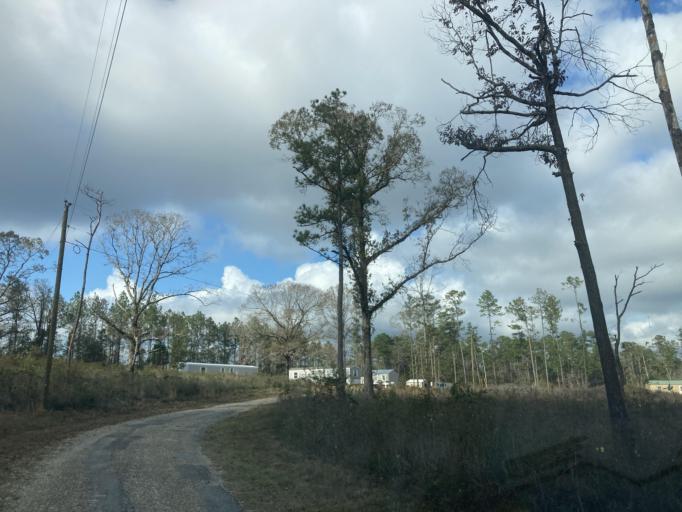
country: US
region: Mississippi
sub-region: Harrison County
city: Saucier
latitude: 30.7316
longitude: -89.0775
